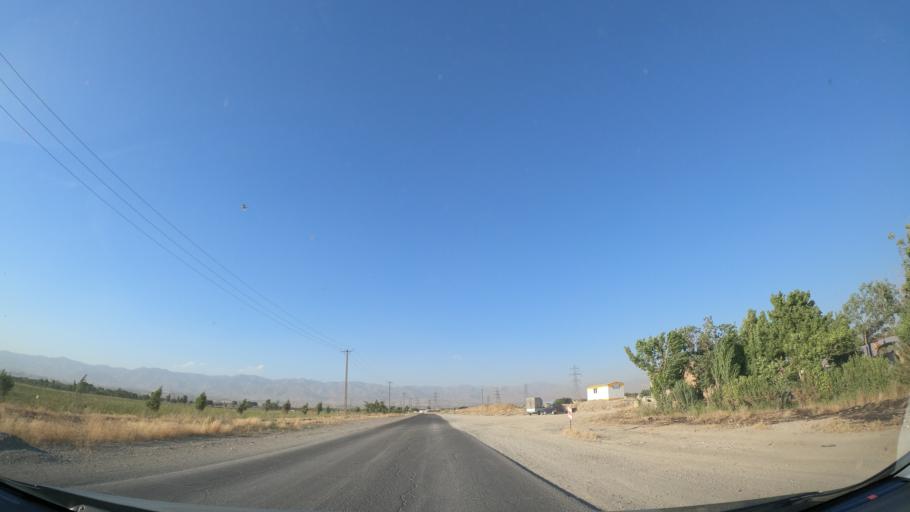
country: IR
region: Alborz
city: Hashtgerd
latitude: 35.9190
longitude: 50.7377
